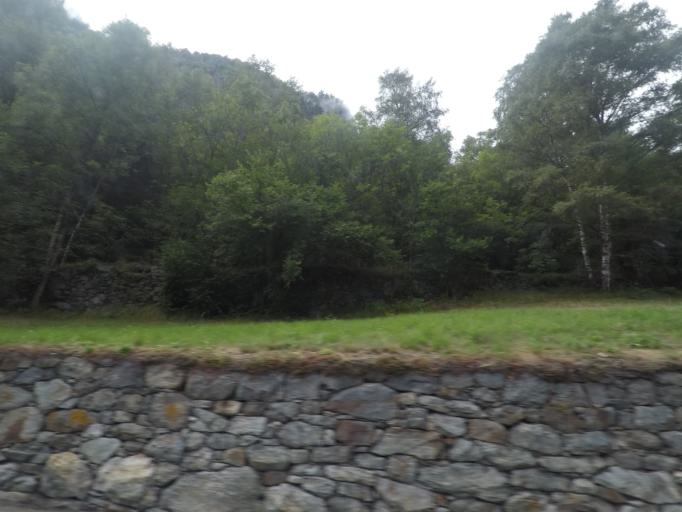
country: IT
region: Aosta Valley
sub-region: Valle d'Aosta
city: Antey-Saint-Andre
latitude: 45.8157
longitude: 7.5877
